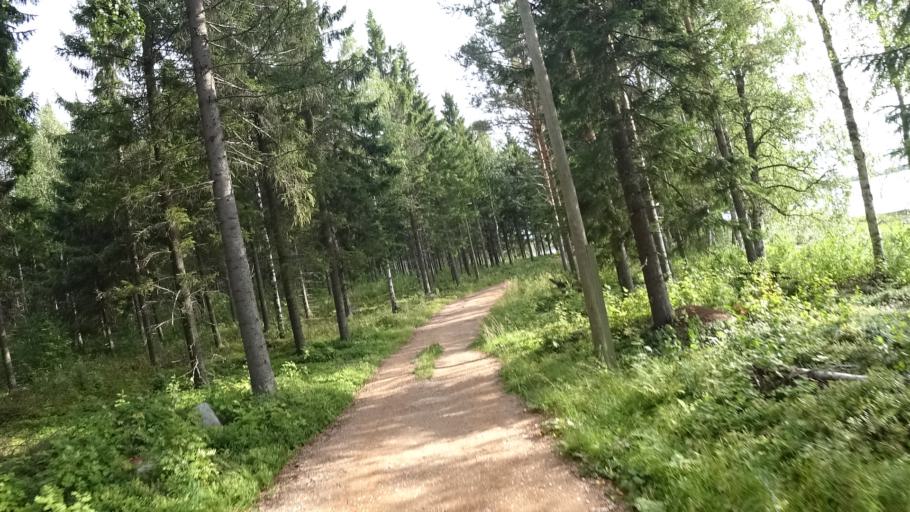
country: FI
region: North Karelia
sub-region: Joensuu
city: Ilomantsi
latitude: 62.6698
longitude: 30.9061
